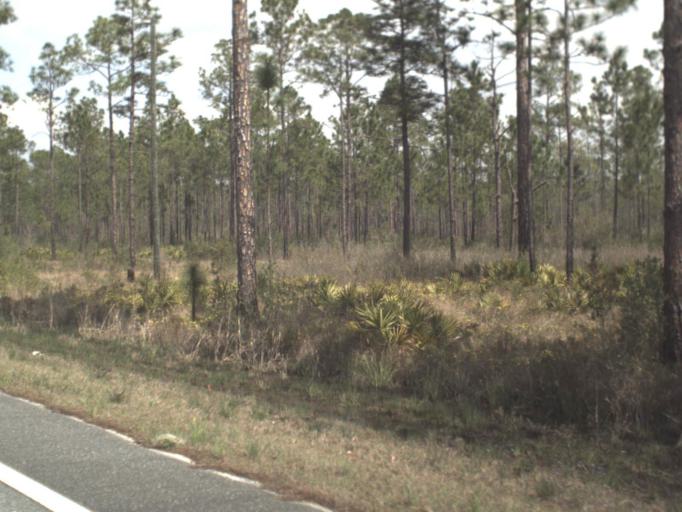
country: US
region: Florida
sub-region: Franklin County
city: Apalachicola
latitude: 29.9379
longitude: -84.9768
